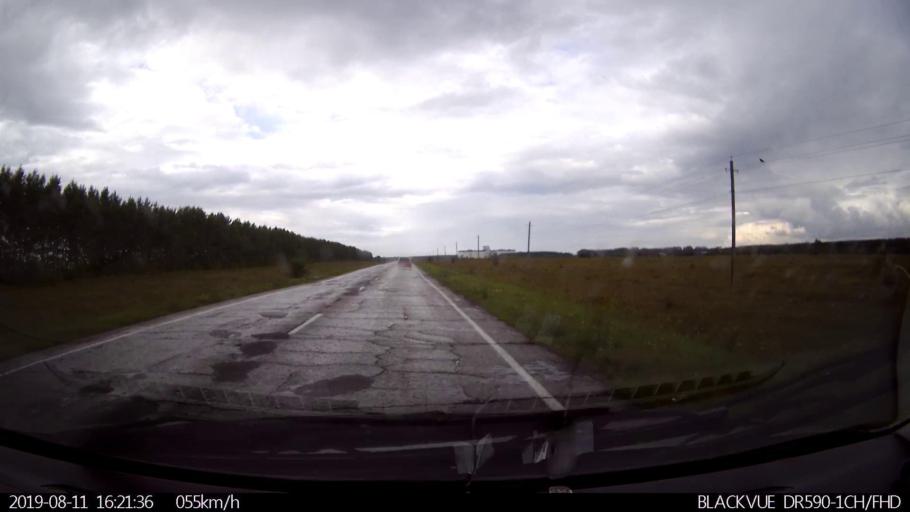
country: RU
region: Ulyanovsk
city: Mayna
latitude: 54.0811
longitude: 47.5971
